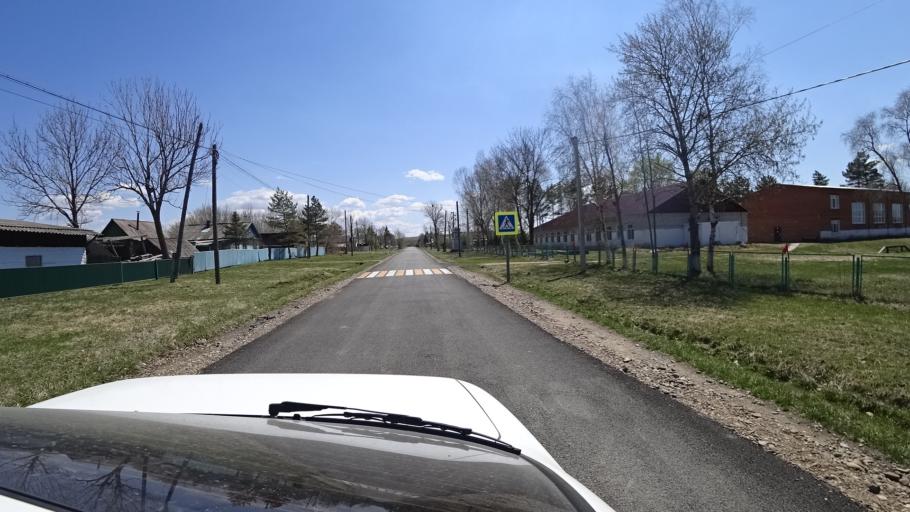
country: RU
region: Primorskiy
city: Dal'nerechensk
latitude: 45.7953
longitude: 133.7683
